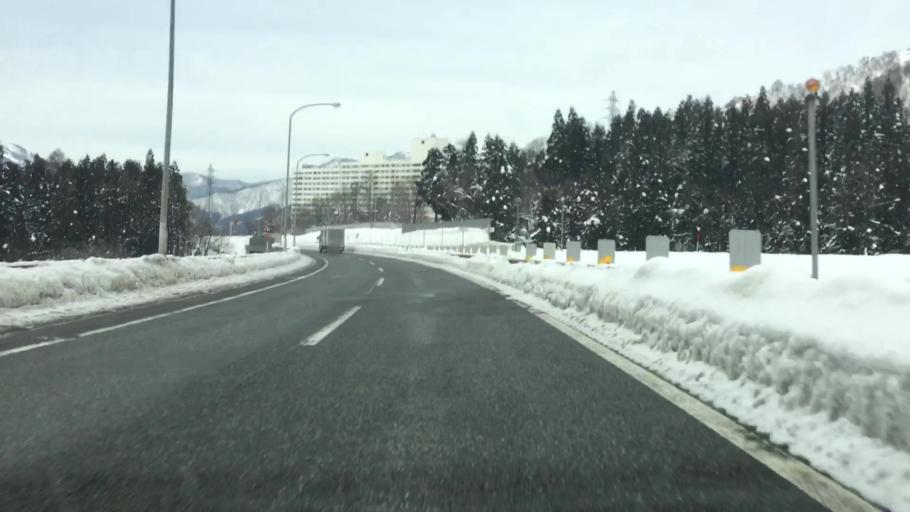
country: JP
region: Niigata
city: Shiozawa
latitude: 36.9006
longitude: 138.8473
